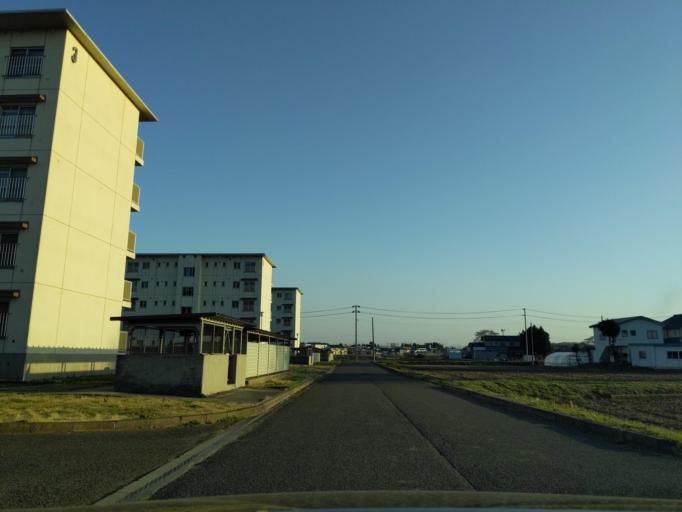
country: JP
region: Fukushima
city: Koriyama
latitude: 37.4057
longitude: 140.3207
